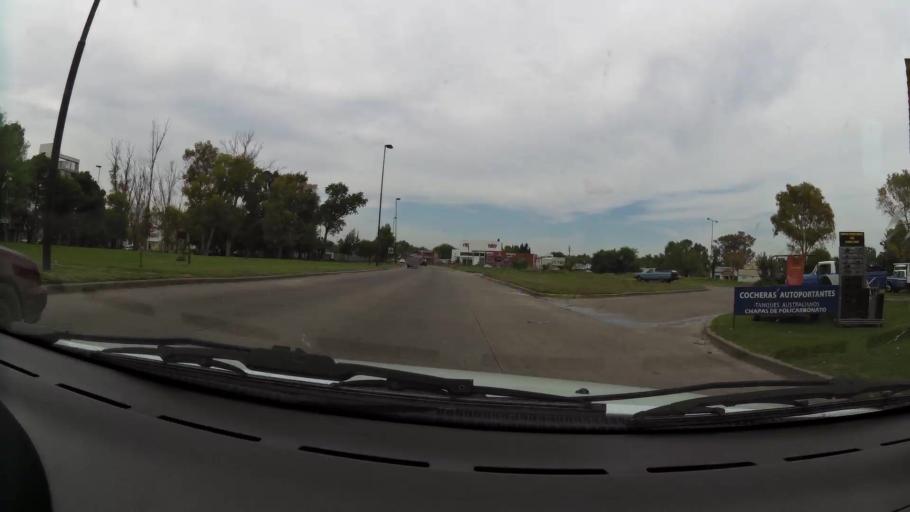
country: AR
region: Buenos Aires
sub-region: Partido de La Plata
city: La Plata
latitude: -34.9254
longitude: -57.9899
